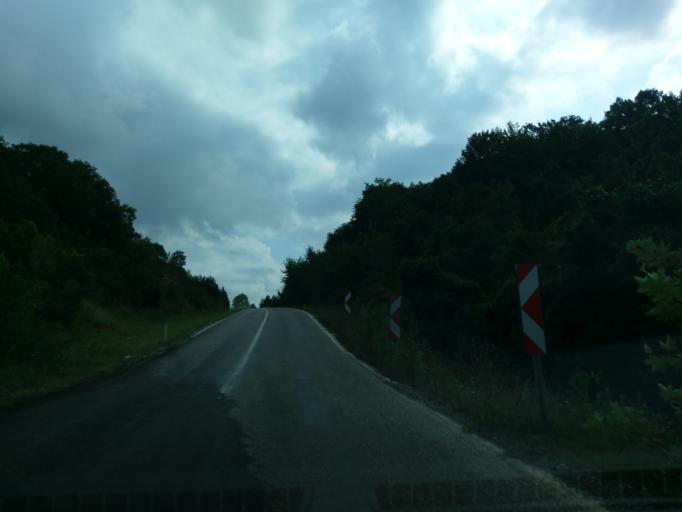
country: TR
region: Sinop
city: Yenikonak
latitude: 41.9456
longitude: 34.7499
